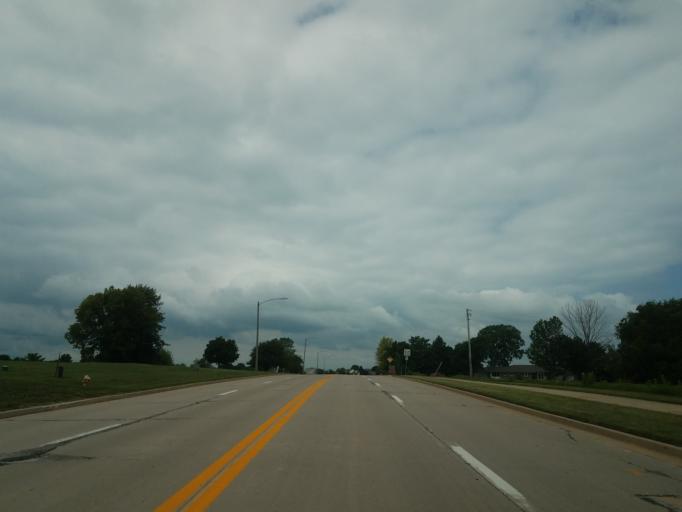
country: US
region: Illinois
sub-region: McLean County
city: Bloomington
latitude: 40.4512
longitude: -89.0354
